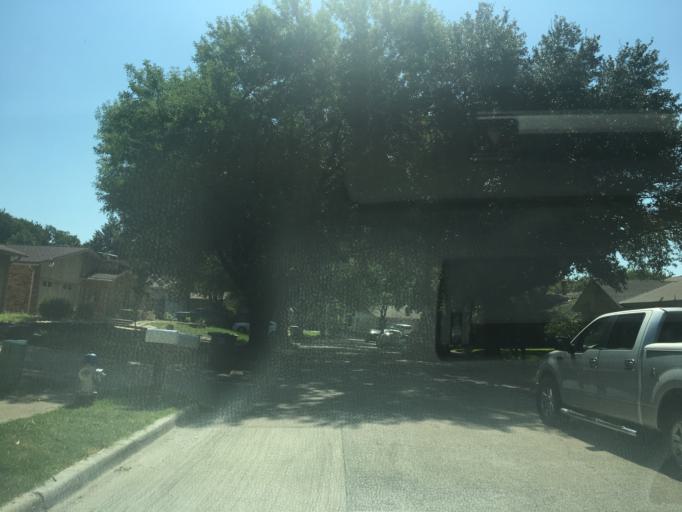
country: US
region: Texas
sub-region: Dallas County
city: Garland
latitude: 32.8557
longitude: -96.6550
